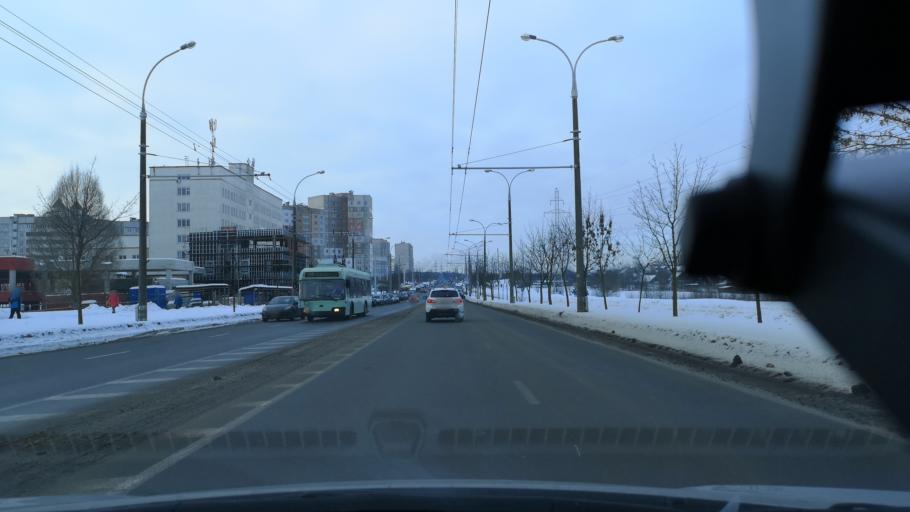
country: BY
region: Minsk
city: Borovlyany
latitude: 53.9519
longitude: 27.6794
